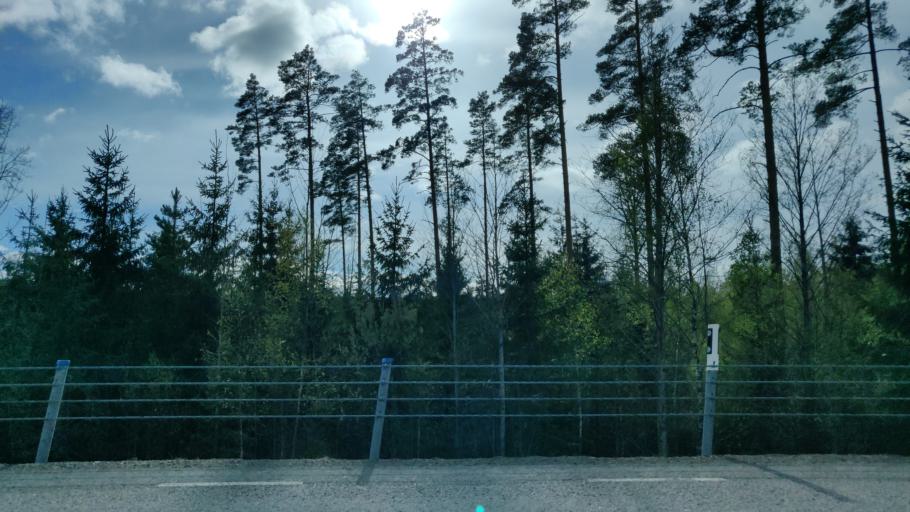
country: SE
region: Vaermland
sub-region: Forshaga Kommun
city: Deje
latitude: 59.5725
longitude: 13.4723
